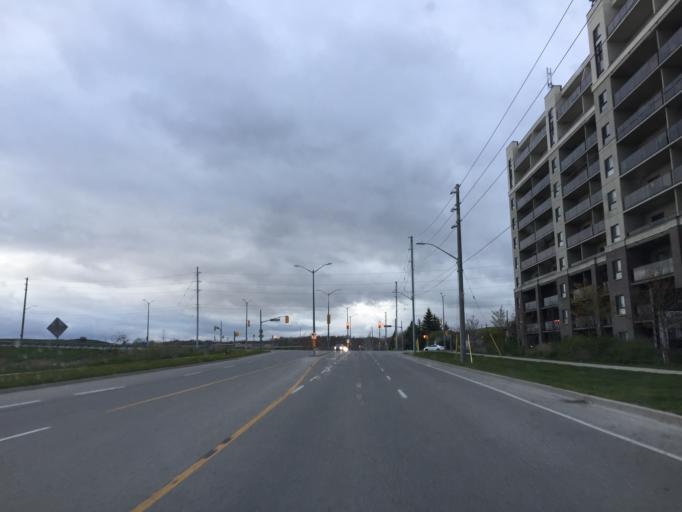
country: CA
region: Ontario
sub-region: Wellington County
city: Guelph
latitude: 43.5212
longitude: -80.2878
